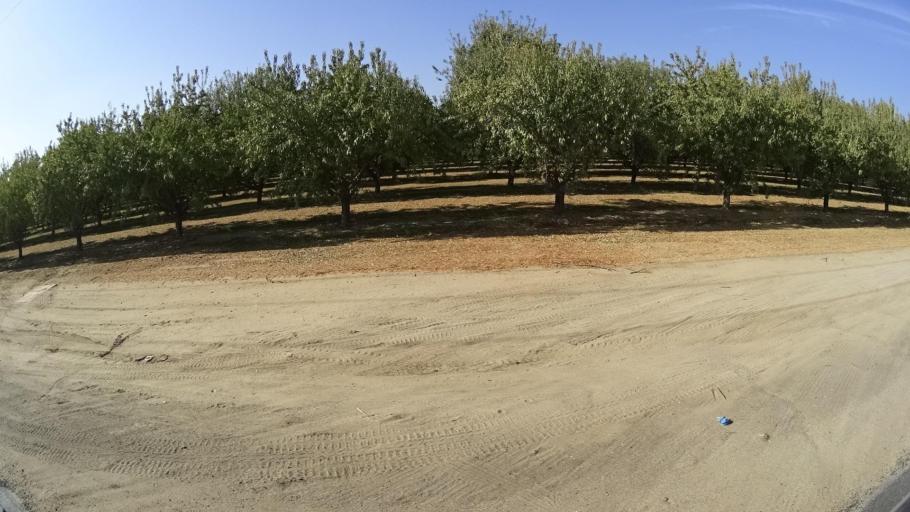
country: US
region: California
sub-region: Kern County
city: Rosedale
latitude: 35.5023
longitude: -119.1524
